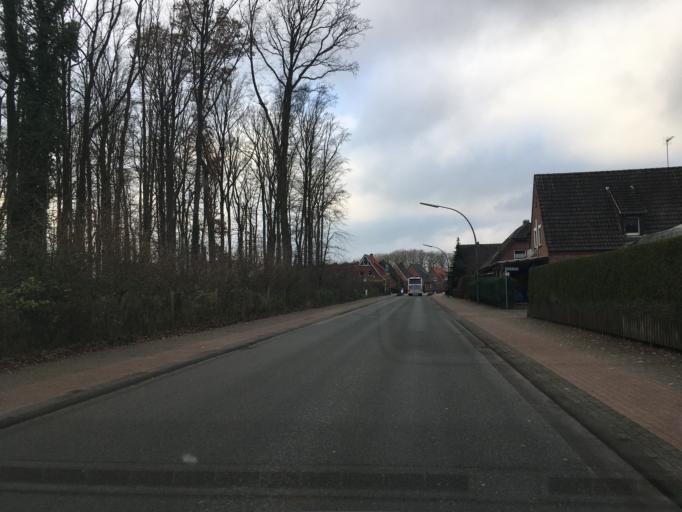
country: DE
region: North Rhine-Westphalia
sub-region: Regierungsbezirk Munster
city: Gescher
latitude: 51.9487
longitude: 7.0037
